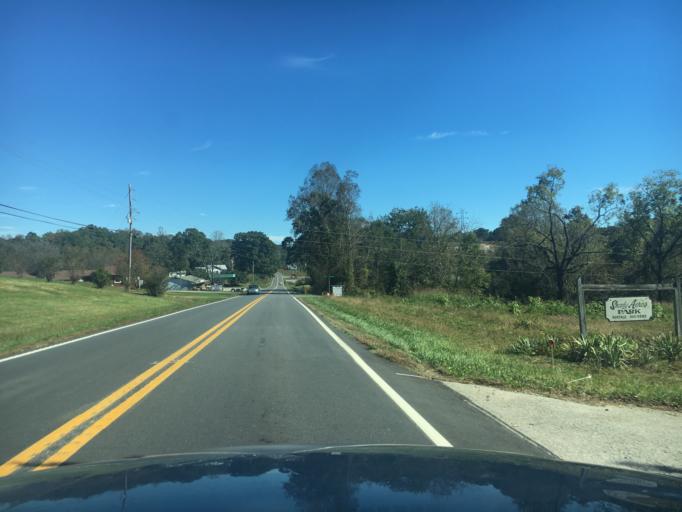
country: US
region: North Carolina
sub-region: Burke County
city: Salem
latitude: 35.6629
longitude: -81.7487
